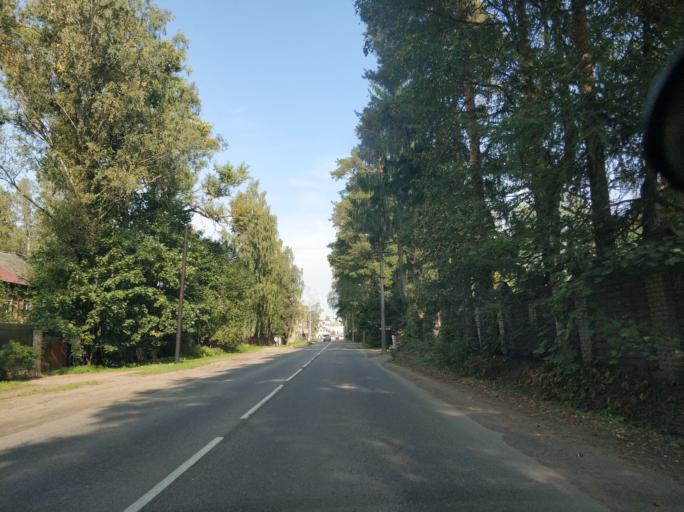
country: RU
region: Leningrad
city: Vsevolozhsk
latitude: 60.0142
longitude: 30.6221
